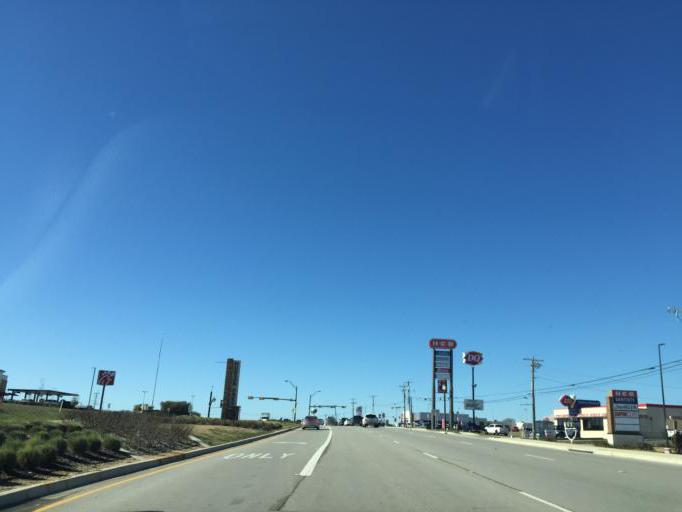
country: US
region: Texas
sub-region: Parker County
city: Hudson Oaks
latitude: 32.7563
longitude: -97.6970
